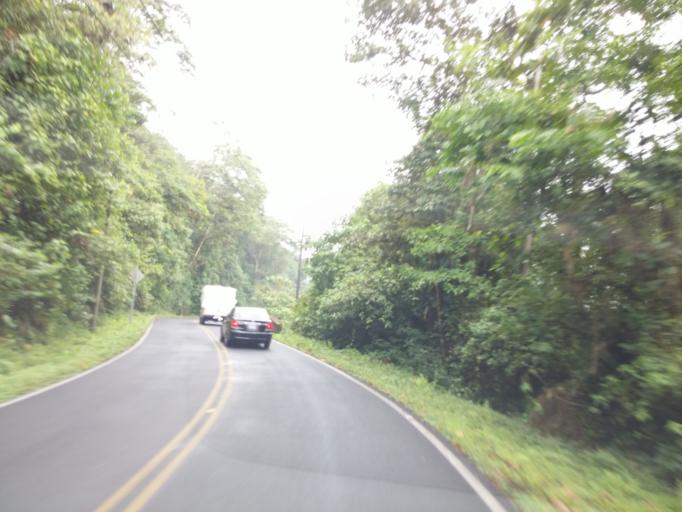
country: CR
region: Alajuela
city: San Ramon
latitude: 10.2221
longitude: -84.5395
